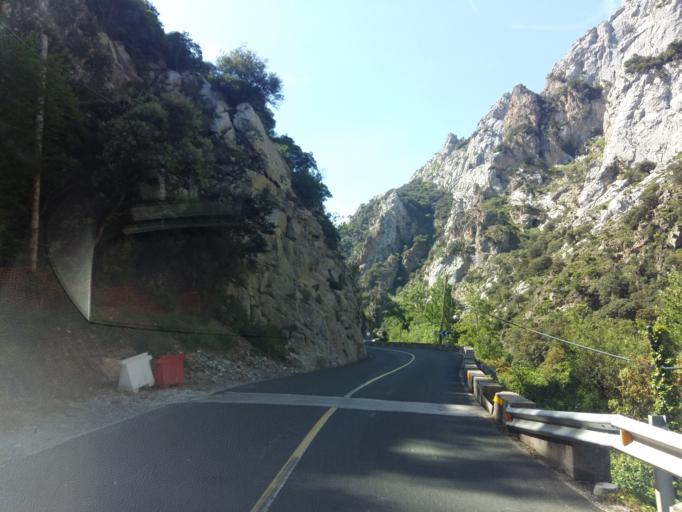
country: ES
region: Cantabria
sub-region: Provincia de Cantabria
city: Potes
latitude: 43.2072
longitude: -4.5943
